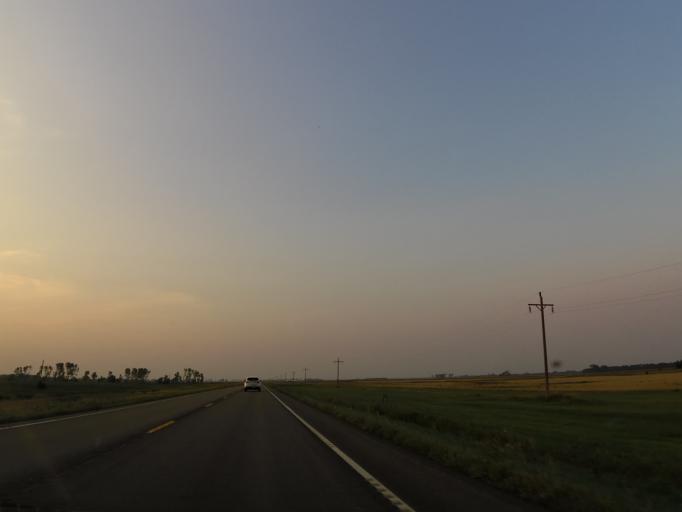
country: US
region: North Dakota
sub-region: Walsh County
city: Park River
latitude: 48.1889
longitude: -97.6226
